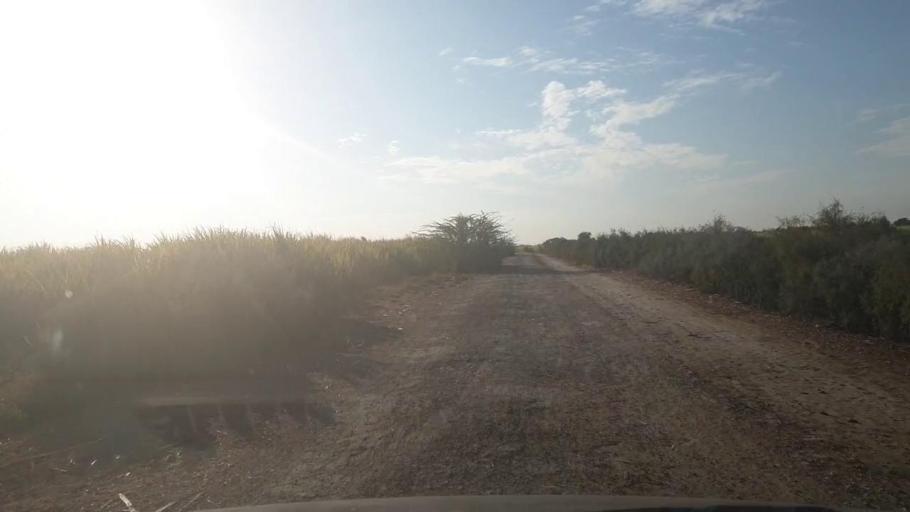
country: PK
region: Sindh
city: Sinjhoro
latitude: 26.0490
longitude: 68.8705
